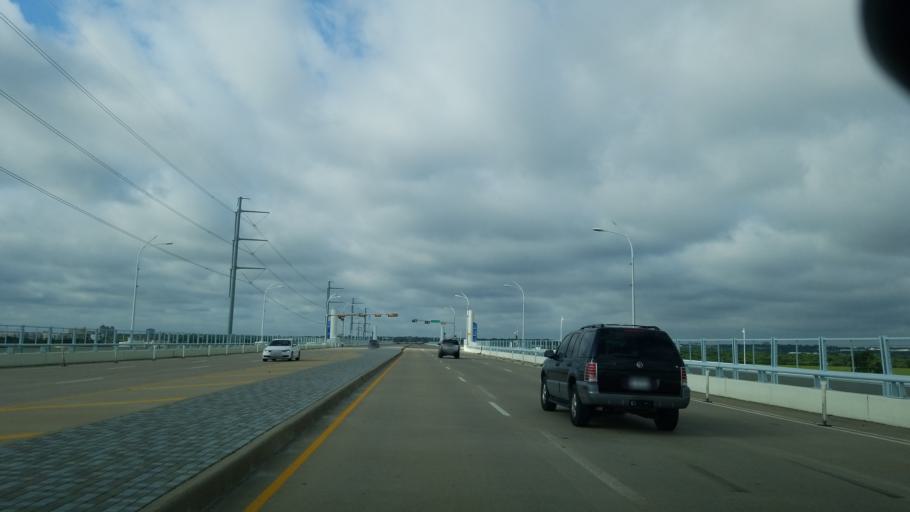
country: US
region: Texas
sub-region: Dallas County
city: Dallas
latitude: 32.7923
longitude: -96.8346
